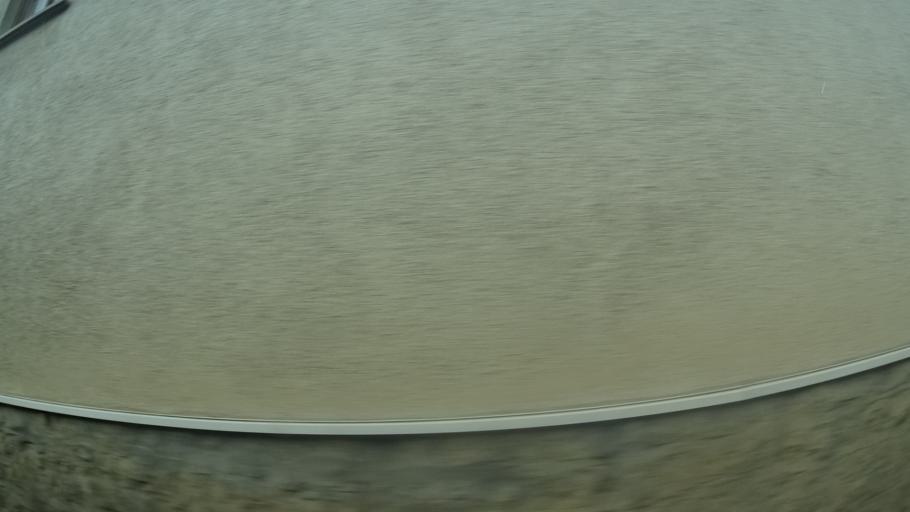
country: DE
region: Hesse
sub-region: Regierungsbezirk Kassel
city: Rasdorf
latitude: 50.7421
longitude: 9.8630
